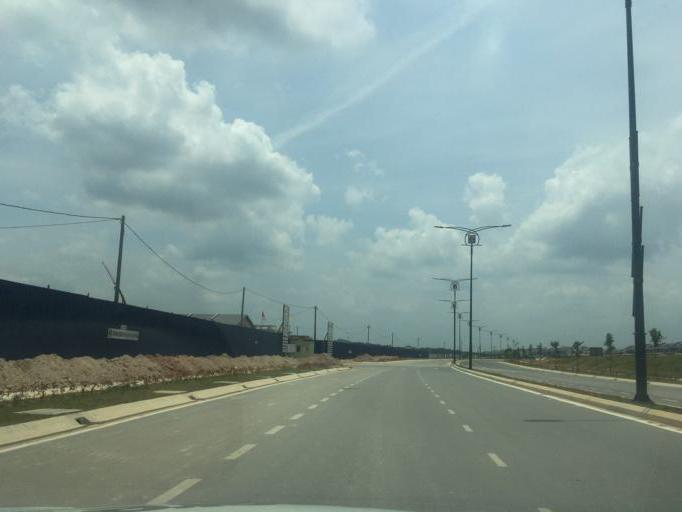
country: MY
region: Putrajaya
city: Putrajaya
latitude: 2.8502
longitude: 101.7051
